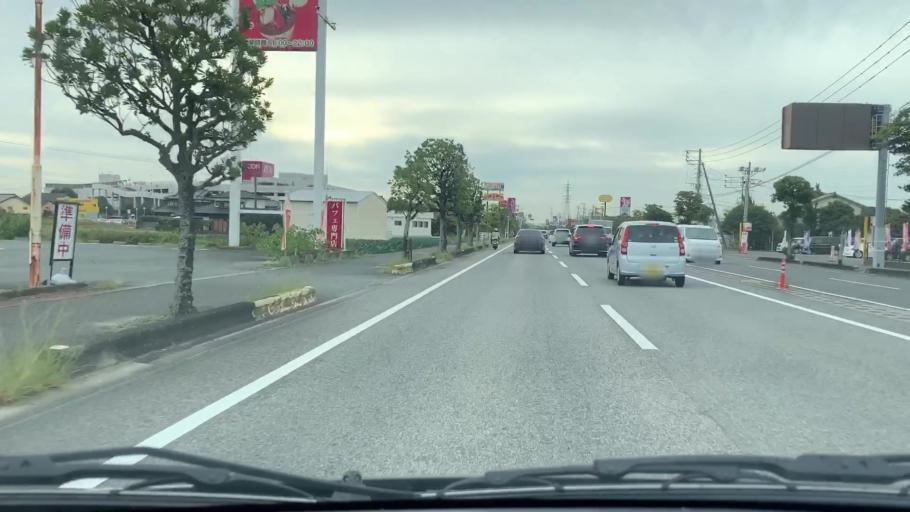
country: JP
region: Saga Prefecture
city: Saga-shi
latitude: 33.3072
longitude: 130.2775
